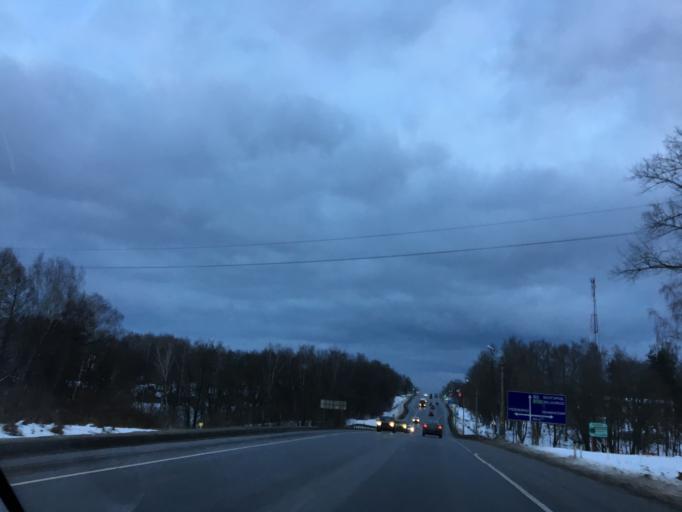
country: RU
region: Tula
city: Barsuki
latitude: 54.3427
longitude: 37.5440
